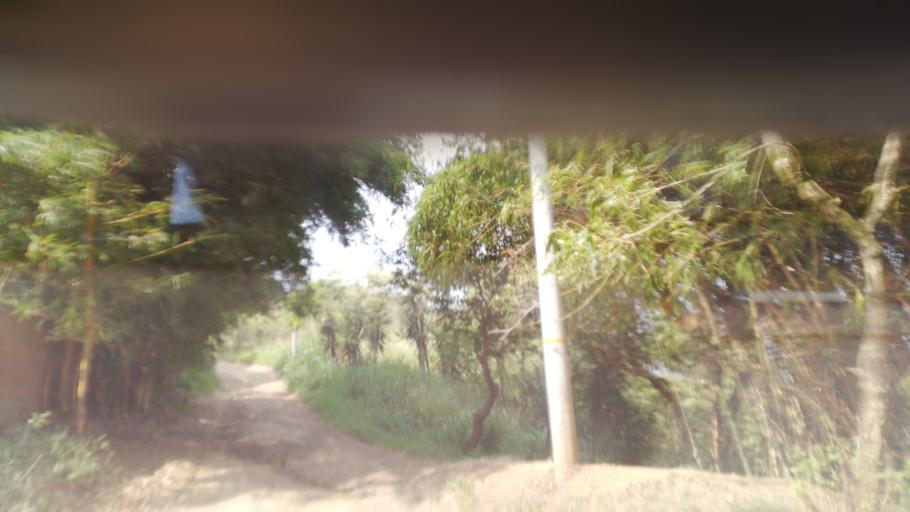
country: CO
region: Valle del Cauca
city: Cali
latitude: 3.4899
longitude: -76.5431
